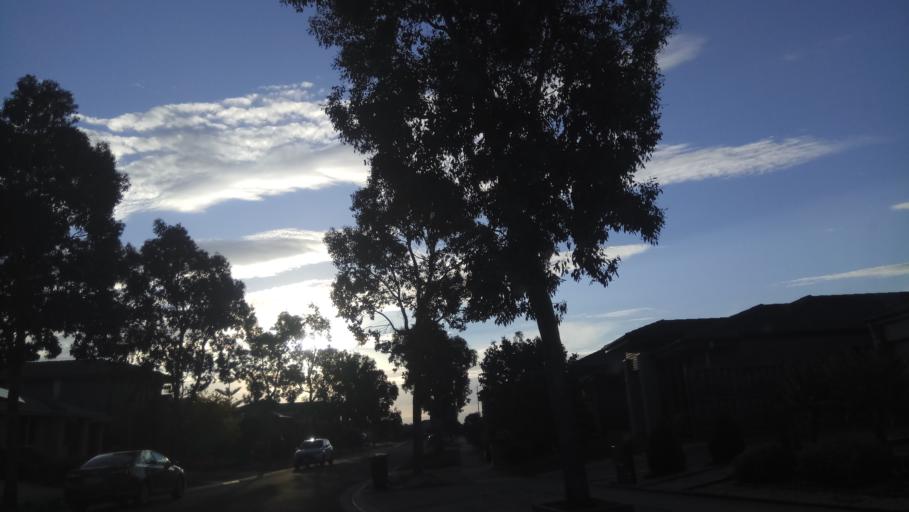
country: AU
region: Victoria
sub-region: Wyndham
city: Point Cook
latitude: -37.9032
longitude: 144.7371
